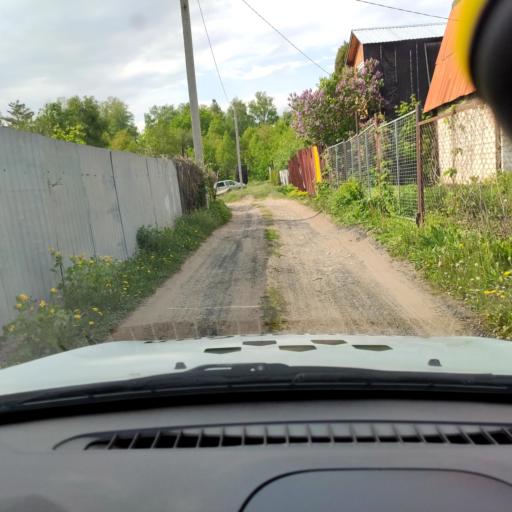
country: RU
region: Samara
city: Zhigulevsk
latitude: 53.5301
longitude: 49.5578
